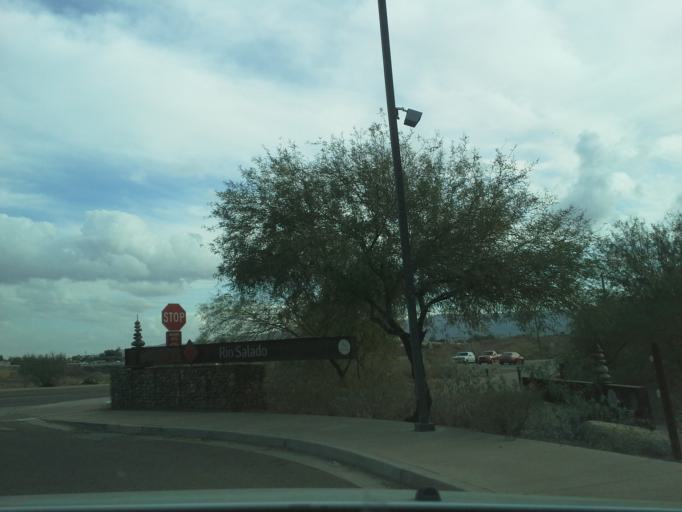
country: US
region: Arizona
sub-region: Maricopa County
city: Phoenix
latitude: 33.4168
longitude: -112.0825
